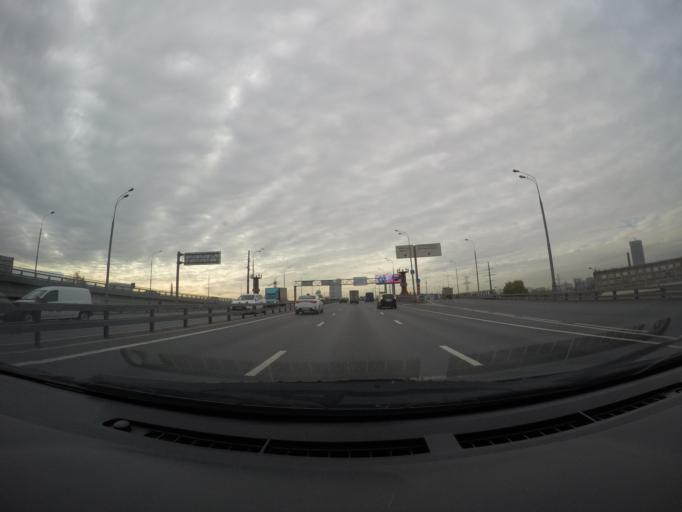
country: RU
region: Moscow
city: Rostokino
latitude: 55.8493
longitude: 37.6745
